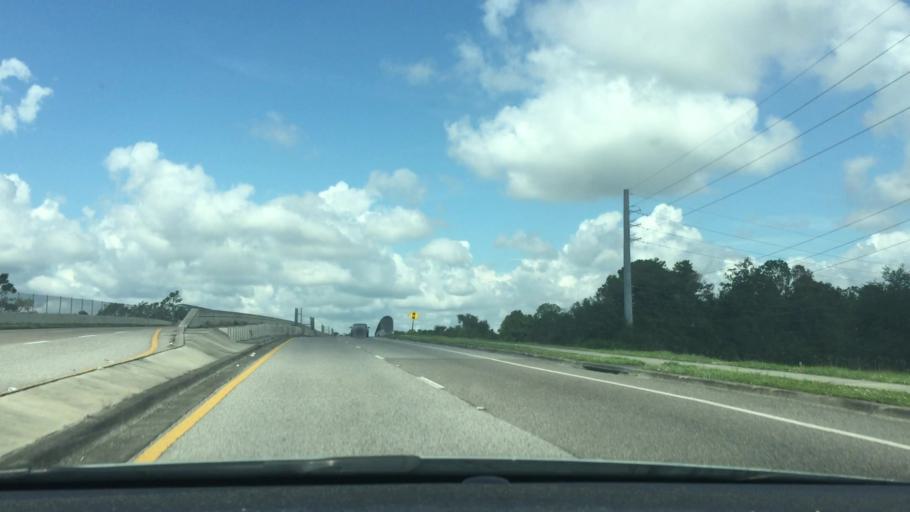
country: US
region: Florida
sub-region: Osceola County
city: Buenaventura Lakes
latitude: 28.3042
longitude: -81.3604
